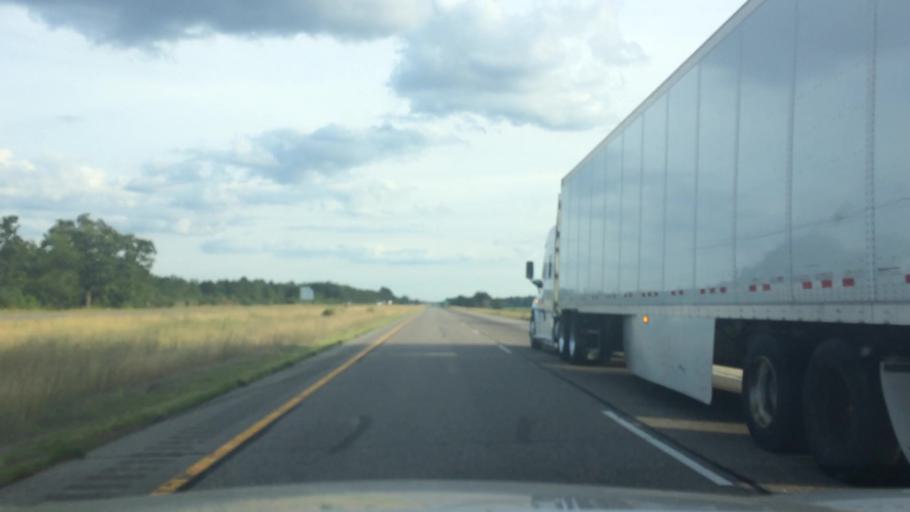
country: US
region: Wisconsin
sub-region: Portage County
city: Plover
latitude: 44.2431
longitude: -89.5243
